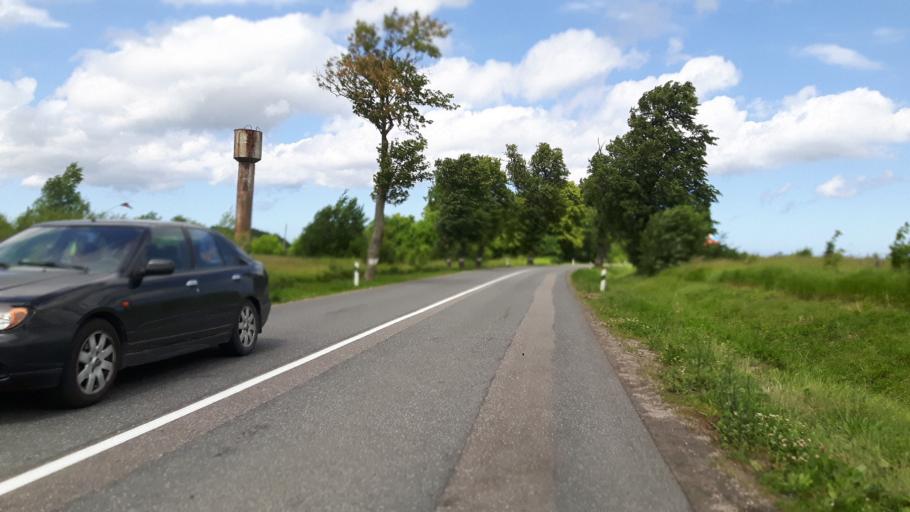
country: RU
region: Kaliningrad
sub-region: Zelenogradskiy Rayon
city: Zelenogradsk
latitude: 54.8875
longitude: 20.4018
